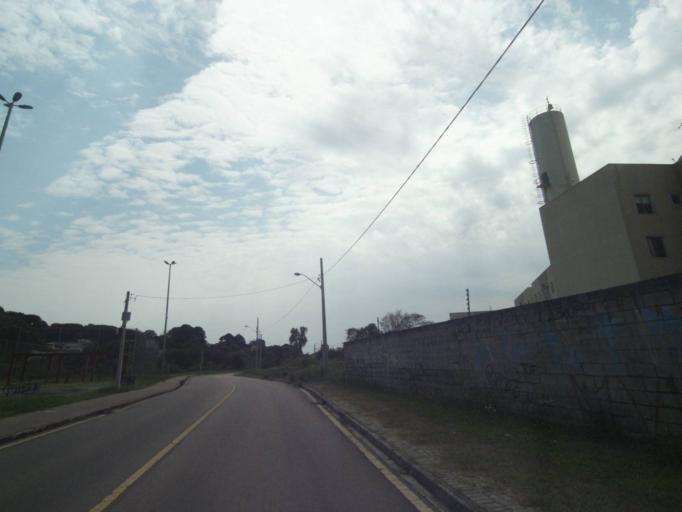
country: BR
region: Parana
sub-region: Curitiba
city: Curitiba
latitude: -25.4741
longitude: -49.3277
